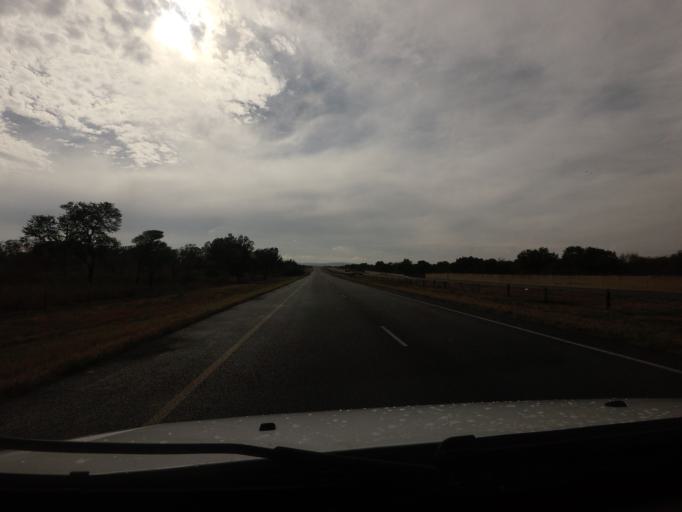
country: ZA
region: Gauteng
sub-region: City of Tshwane Metropolitan Municipality
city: Cullinan
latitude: -25.7642
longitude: 28.3845
